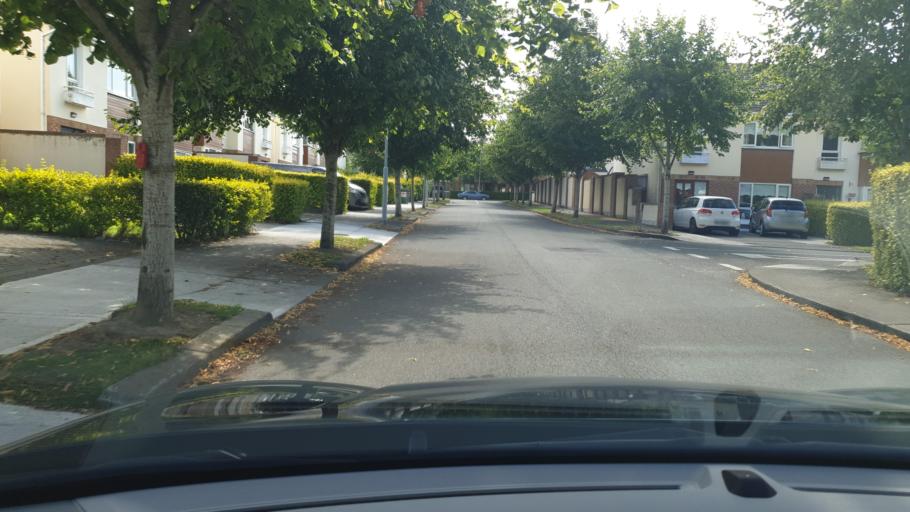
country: IE
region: Leinster
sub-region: An Mhi
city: Dunboyne
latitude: 53.4150
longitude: -6.4808
